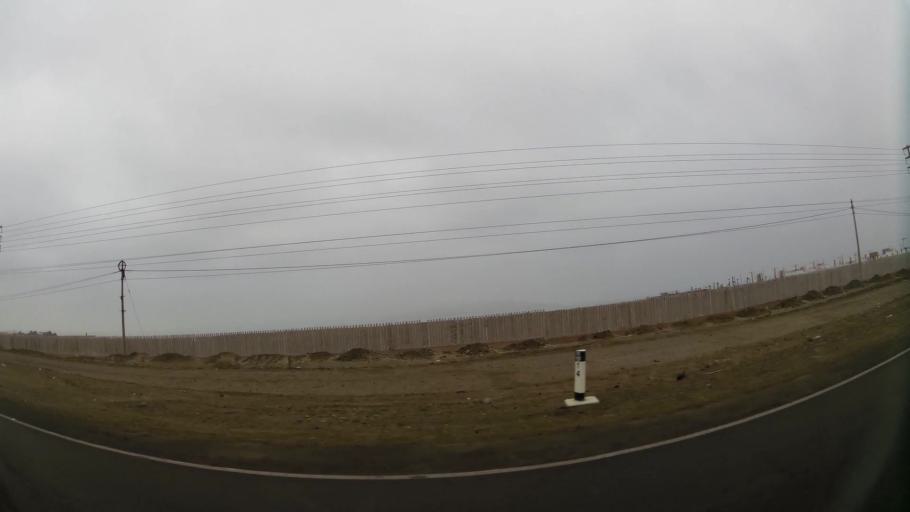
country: PE
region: Ica
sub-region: Provincia de Pisco
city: Paracas
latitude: -13.8121
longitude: -76.2425
